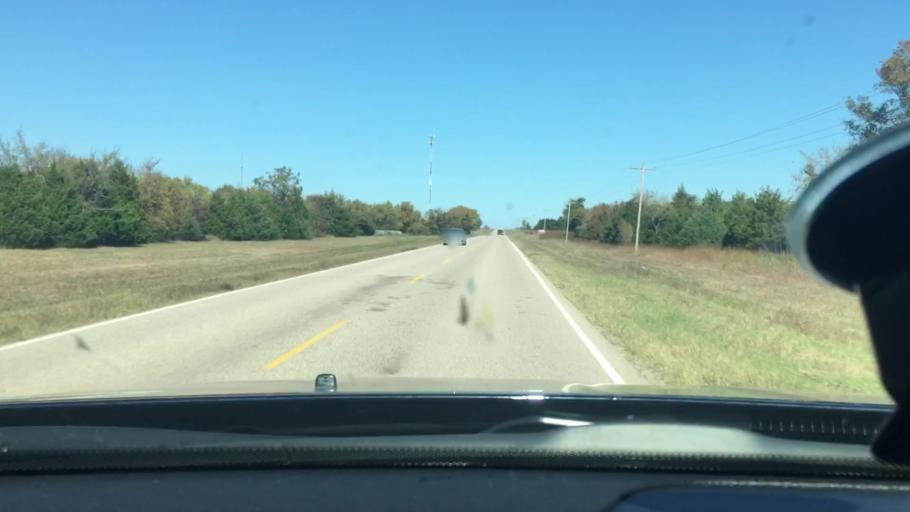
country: US
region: Oklahoma
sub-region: Johnston County
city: Tishomingo
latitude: 34.4242
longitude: -96.6359
